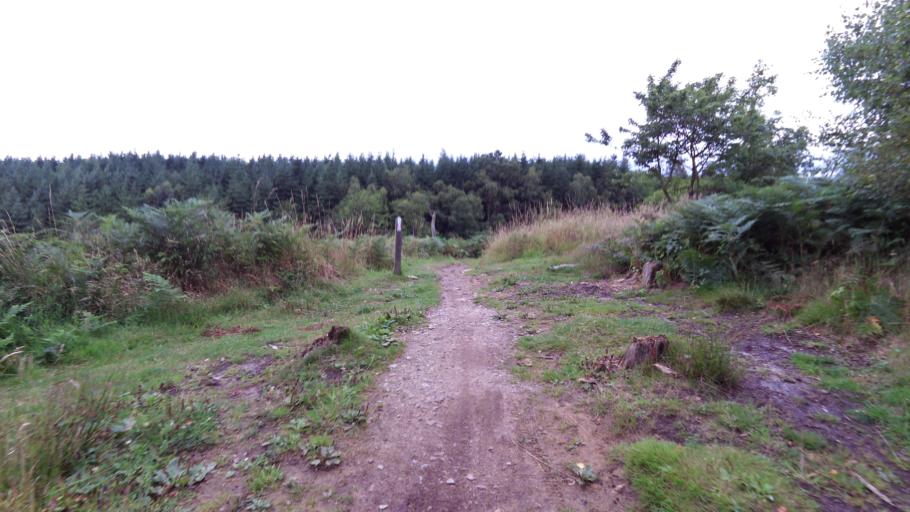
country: GB
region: England
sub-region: North Yorkshire
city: Thornton Dale
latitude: 54.2872
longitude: -0.6873
